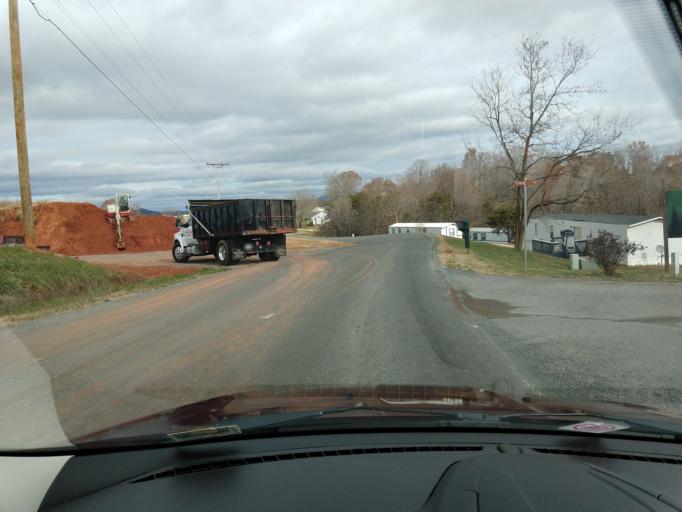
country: US
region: Virginia
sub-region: Franklin County
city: North Shore
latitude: 37.2020
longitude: -79.6858
